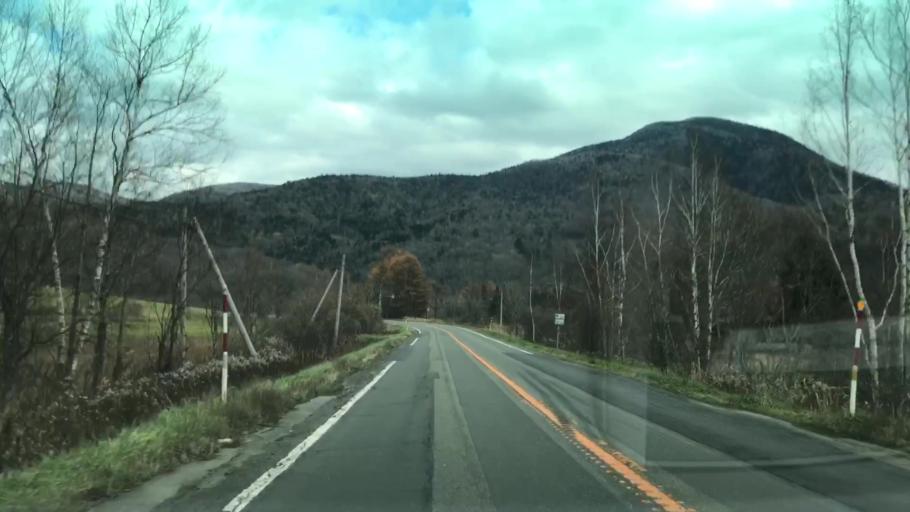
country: JP
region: Hokkaido
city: Shizunai-furukawacho
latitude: 42.8120
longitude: 142.4121
